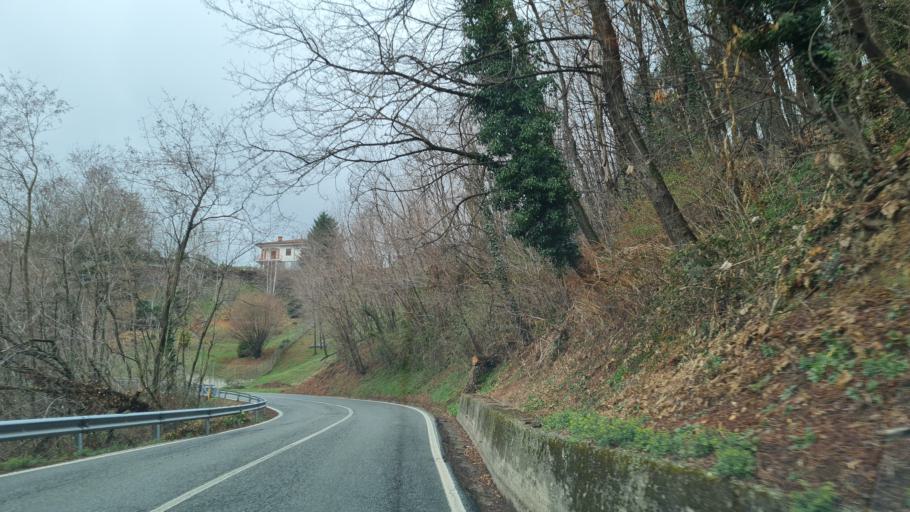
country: IT
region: Piedmont
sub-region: Provincia di Biella
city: Muzzano
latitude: 45.5672
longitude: 7.9901
